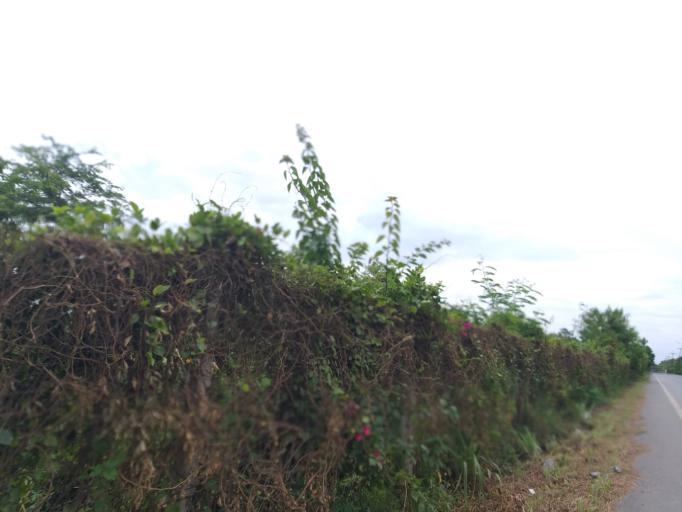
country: TH
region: Pathum Thani
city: Nong Suea
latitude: 14.0582
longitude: 100.8713
